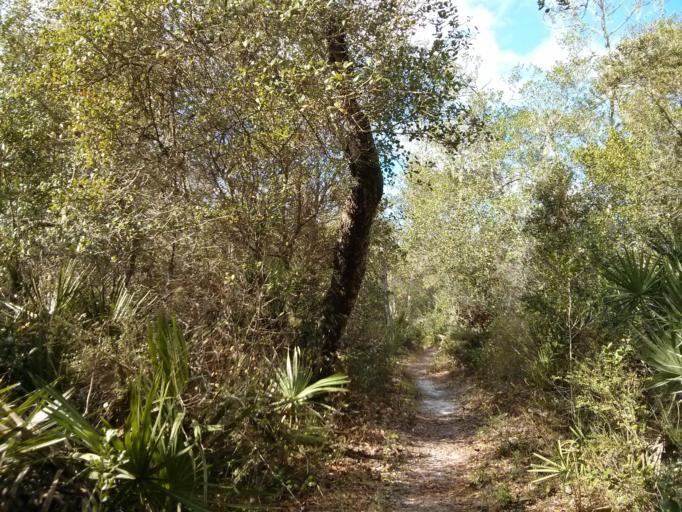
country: US
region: Florida
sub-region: Lake County
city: Astor
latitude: 29.0734
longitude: -81.6282
